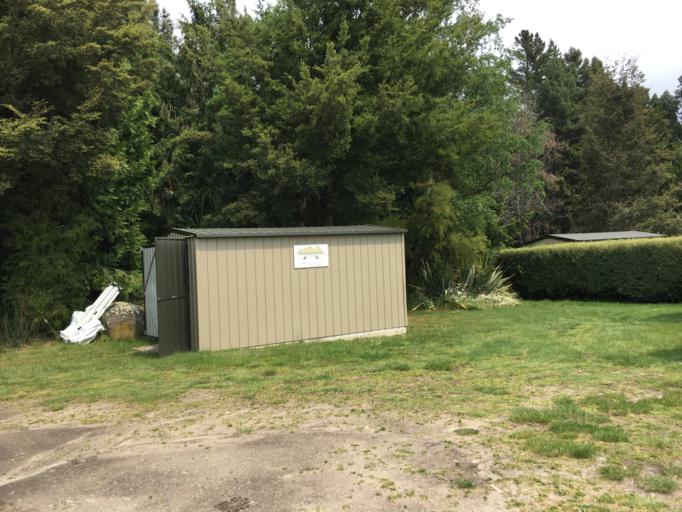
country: NZ
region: Otago
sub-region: Queenstown-Lakes District
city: Queenstown
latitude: -45.0458
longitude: 168.6914
